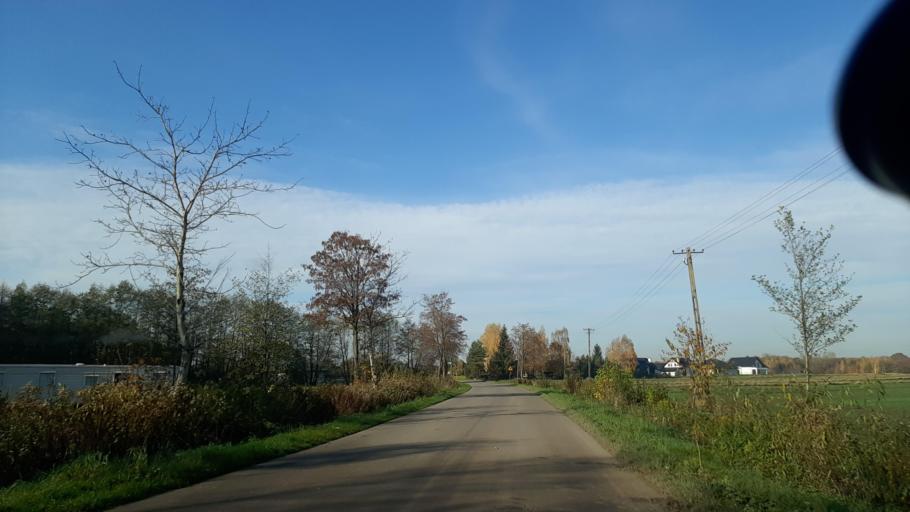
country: PL
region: Lublin Voivodeship
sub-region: Powiat lubelski
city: Jastkow
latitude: 51.3421
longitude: 22.4636
